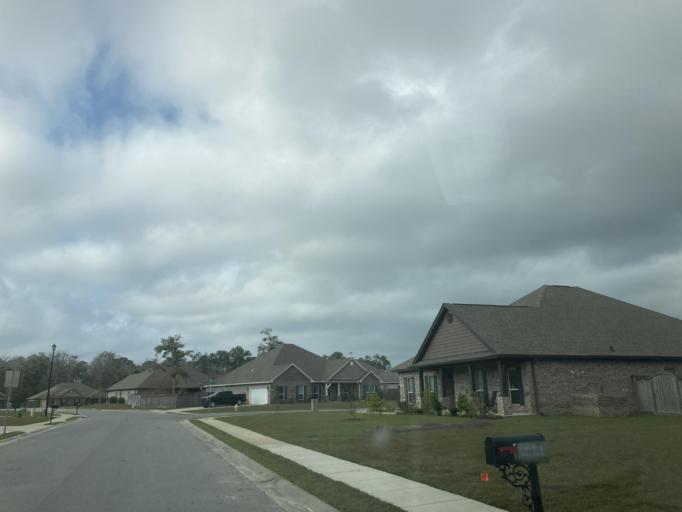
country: US
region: Mississippi
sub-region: Harrison County
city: D'Iberville
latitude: 30.4763
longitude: -88.9819
